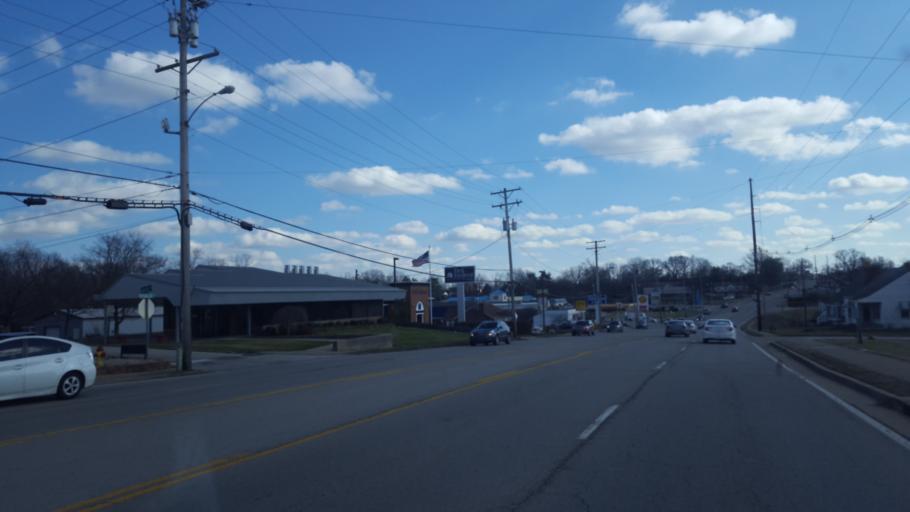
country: US
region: Kentucky
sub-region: Franklin County
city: Frankfort
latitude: 38.2033
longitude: -84.8341
